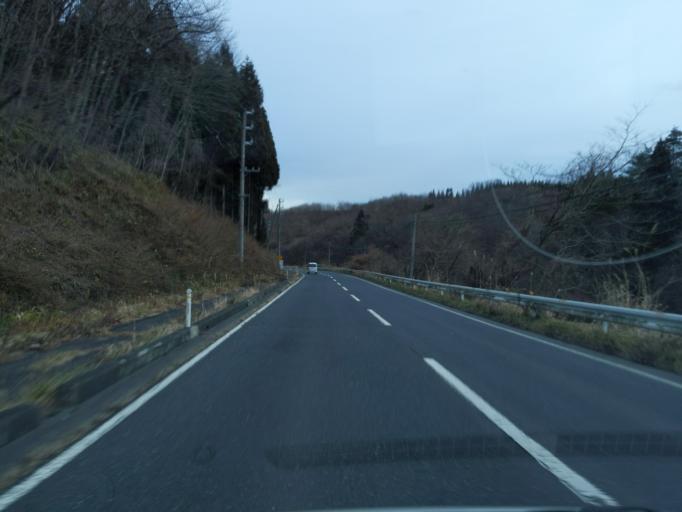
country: JP
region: Iwate
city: Mizusawa
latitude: 39.0288
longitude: 141.3093
